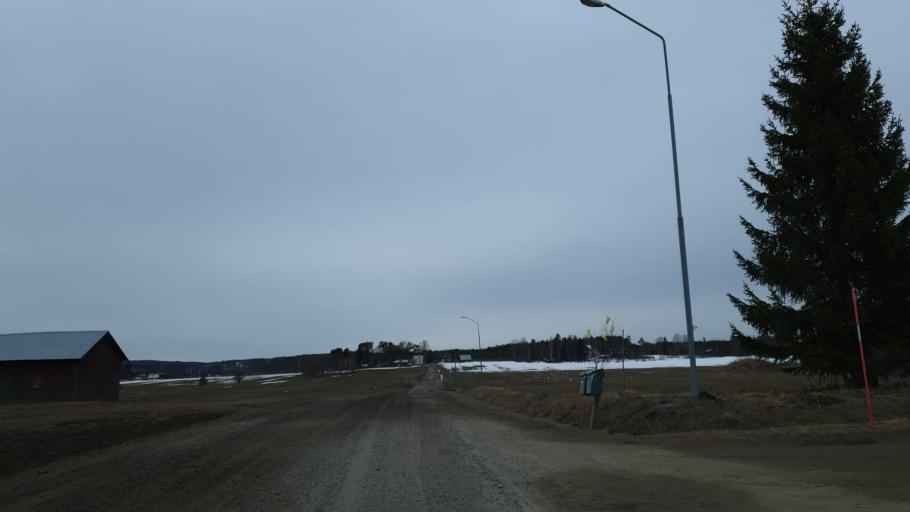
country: SE
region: Vaesterbotten
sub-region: Robertsfors Kommun
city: Robertsfors
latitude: 64.3807
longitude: 20.9152
